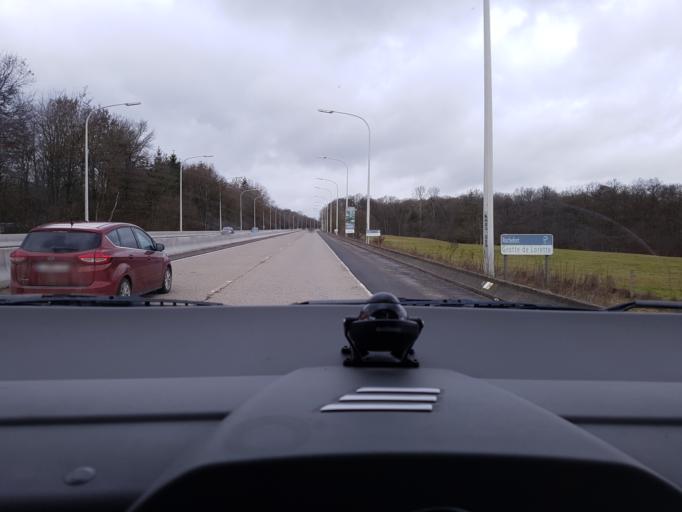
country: BE
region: Wallonia
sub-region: Province du Luxembourg
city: Marche-en-Famenne
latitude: 50.2541
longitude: 5.2723
